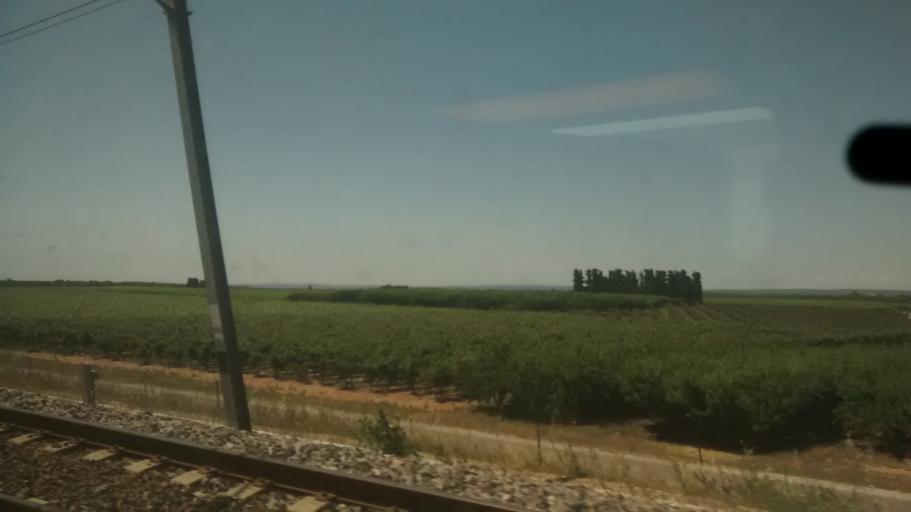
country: FR
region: Languedoc-Roussillon
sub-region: Departement du Gard
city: Jonquieres-Saint-Vincent
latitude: 43.8357
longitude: 4.5357
